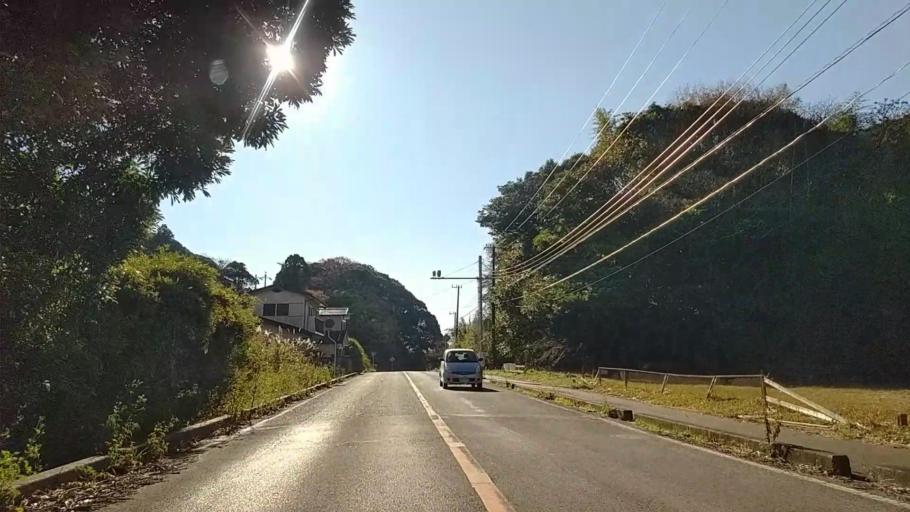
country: JP
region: Chiba
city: Kimitsu
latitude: 35.2651
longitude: 139.8738
